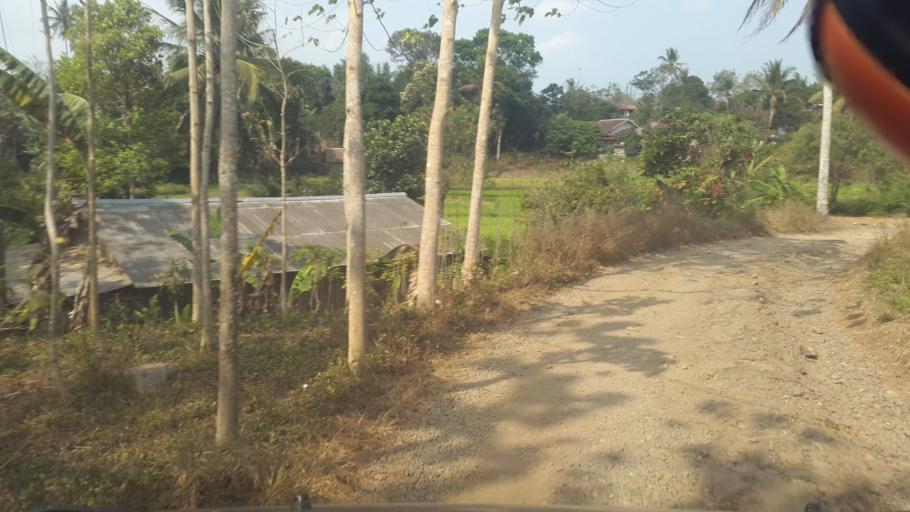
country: ID
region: West Java
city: Nangerang
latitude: -7.1113
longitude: 106.7969
